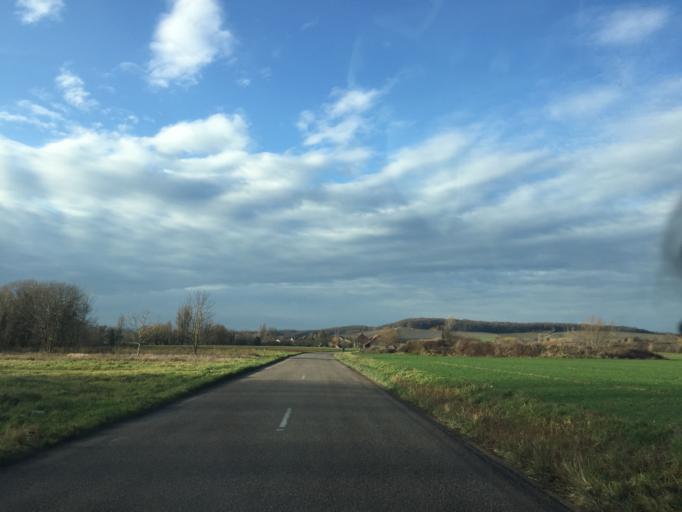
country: FR
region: Franche-Comte
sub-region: Departement du Jura
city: Arbois
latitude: 46.9170
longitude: 5.7611
